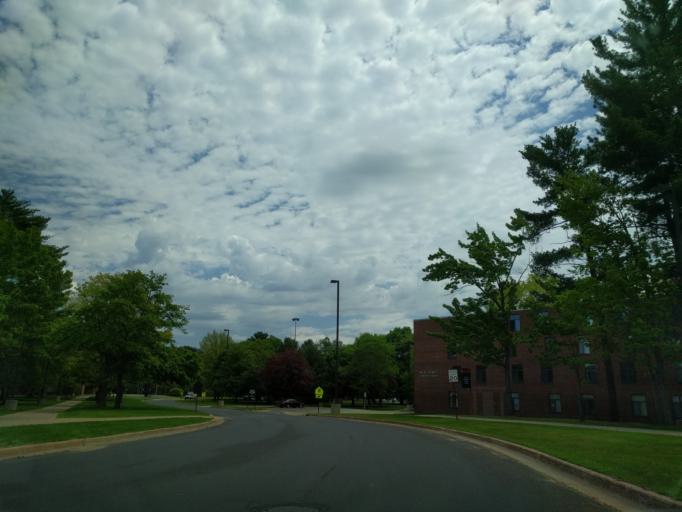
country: US
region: Michigan
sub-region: Marquette County
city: Marquette
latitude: 46.5577
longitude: -87.4026
